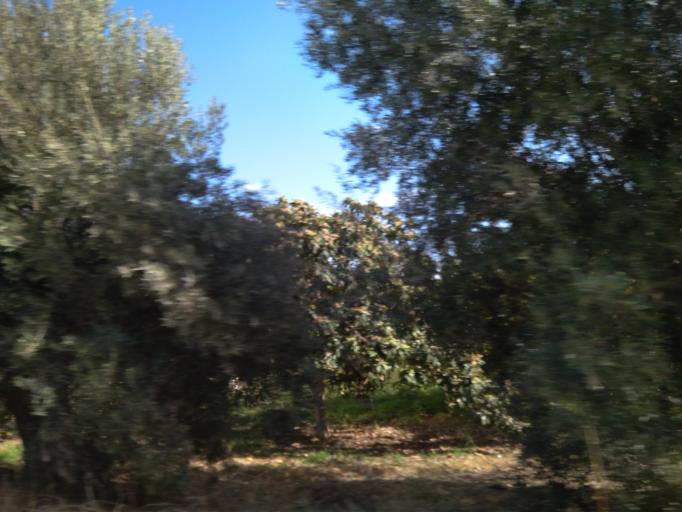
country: PT
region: Faro
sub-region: Faro
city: Santa Barbara de Nexe
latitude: 37.0734
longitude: -7.9595
